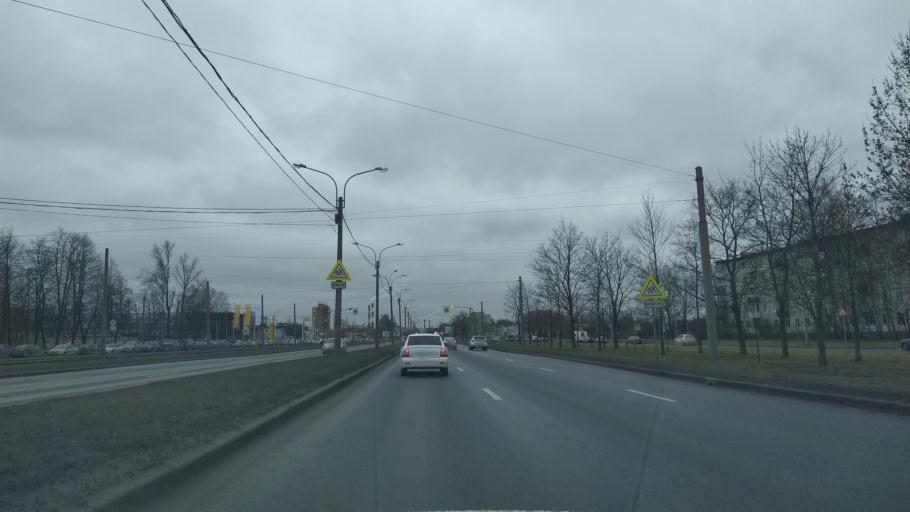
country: RU
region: St.-Petersburg
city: Grazhdanka
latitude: 60.0102
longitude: 30.4344
